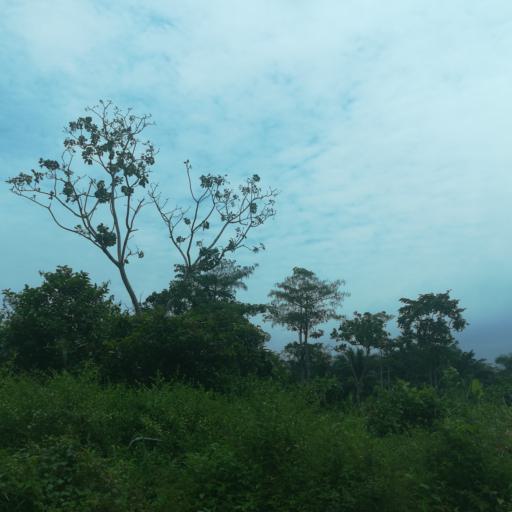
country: NG
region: Lagos
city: Ejirin
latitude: 6.6637
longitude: 3.7933
